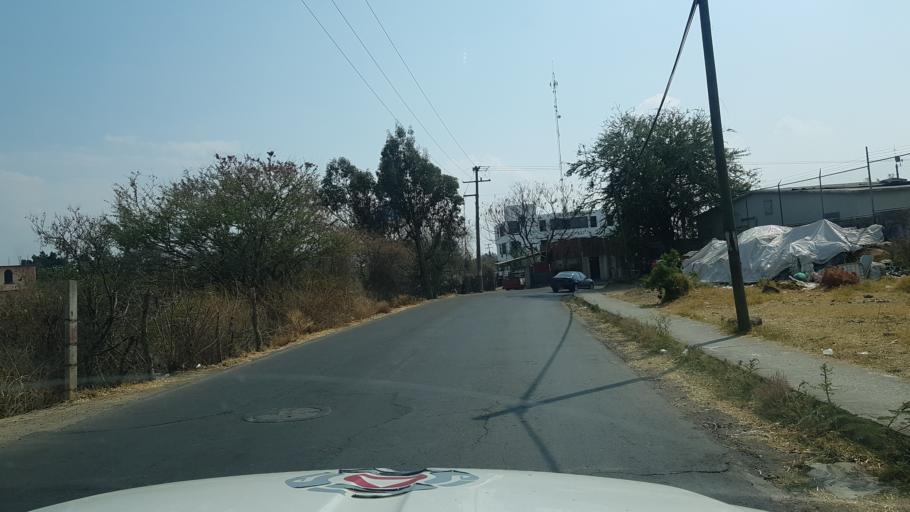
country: MX
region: Morelos
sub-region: Yecapixtla
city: Yecapixtla
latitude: 18.8843
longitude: -98.8672
